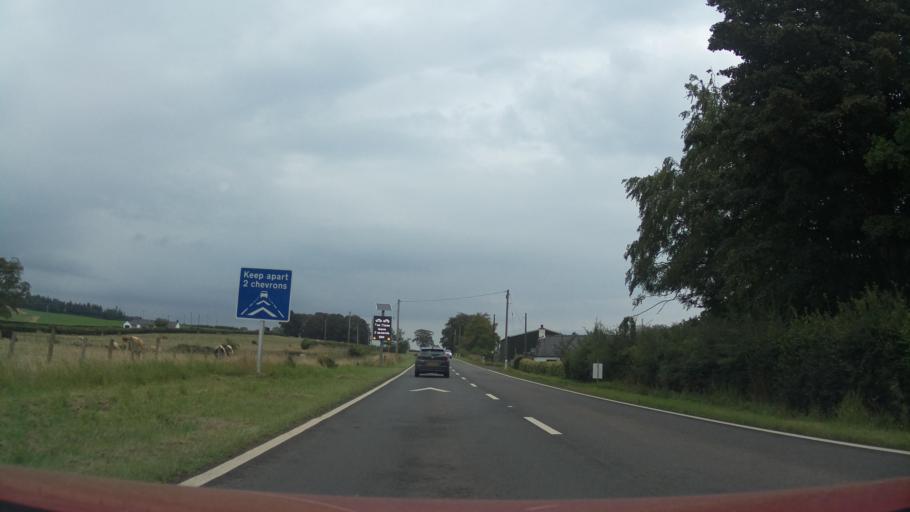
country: GB
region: Scotland
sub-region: Dumfries and Galloway
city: Locharbriggs
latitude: 55.1348
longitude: -3.5628
